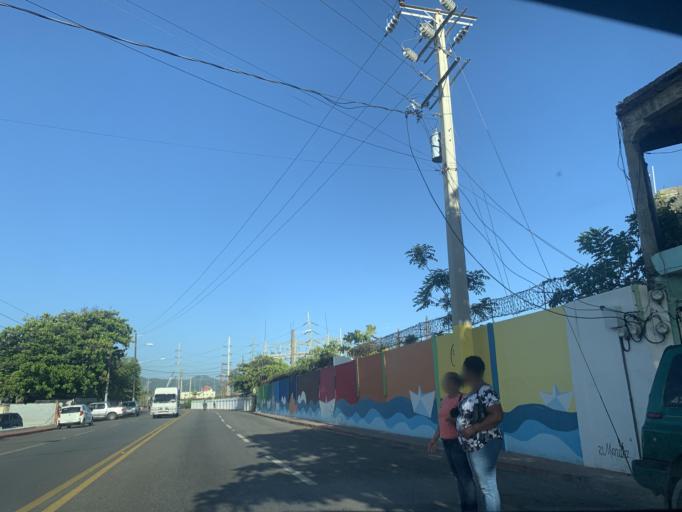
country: DO
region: Puerto Plata
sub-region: Puerto Plata
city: Puerto Plata
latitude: 19.8011
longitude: -70.6936
